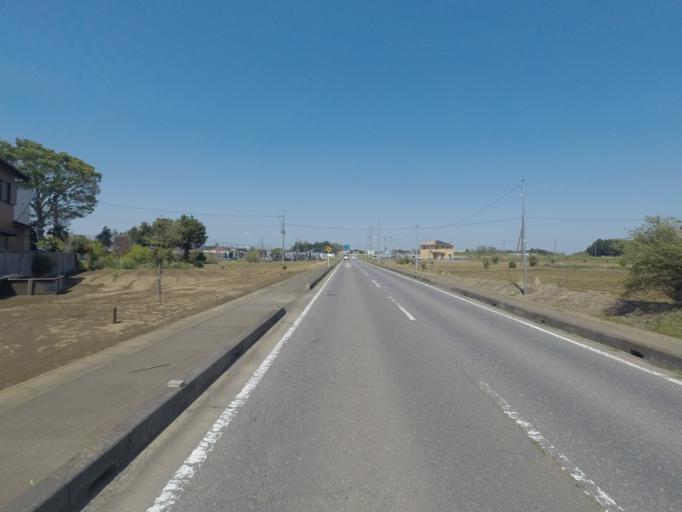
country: JP
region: Ibaraki
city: Ushiku
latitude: 35.9747
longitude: 140.0969
